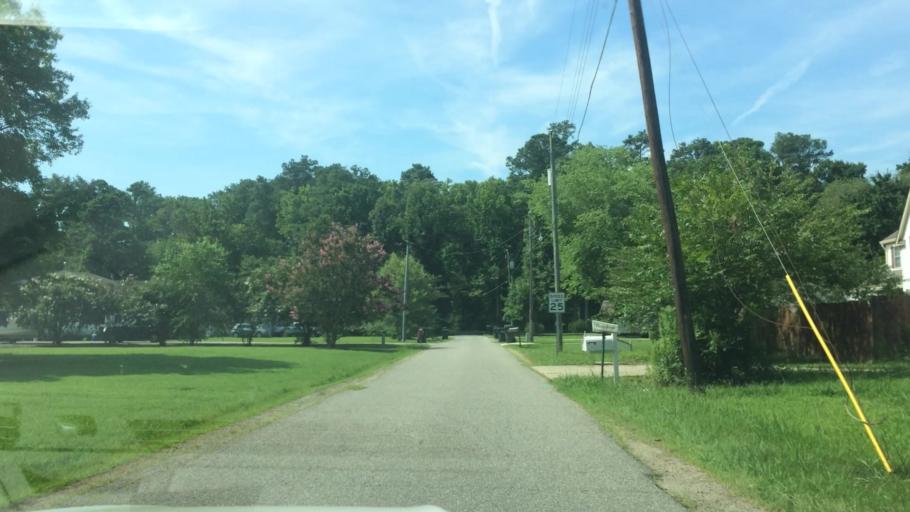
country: US
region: Virginia
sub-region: City of Poquoson
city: Poquoson
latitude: 37.1622
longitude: -76.4261
